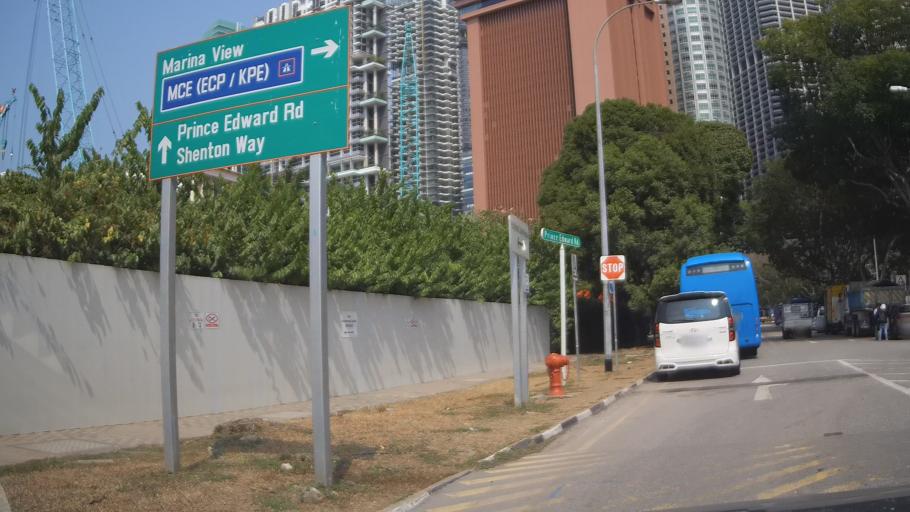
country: SG
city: Singapore
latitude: 1.2742
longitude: 103.8492
